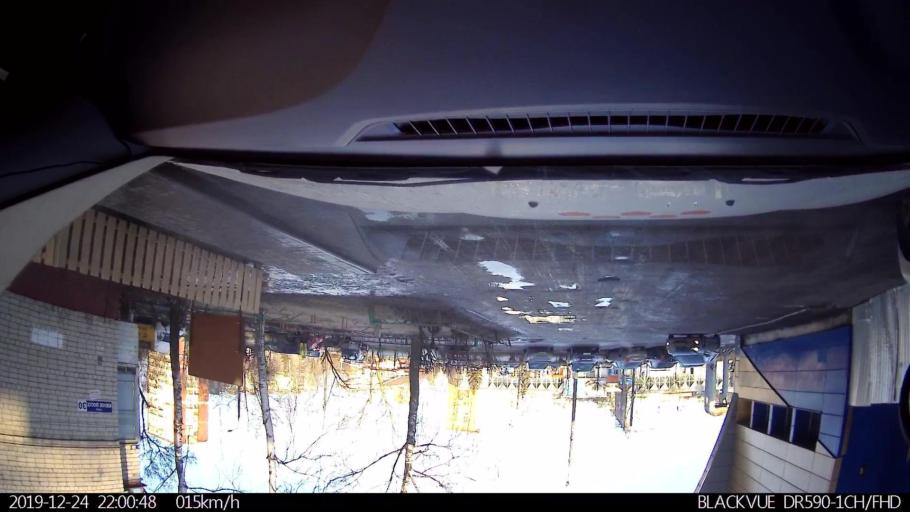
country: RU
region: Nizjnij Novgorod
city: Burevestnik
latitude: 56.2269
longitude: 43.8657
